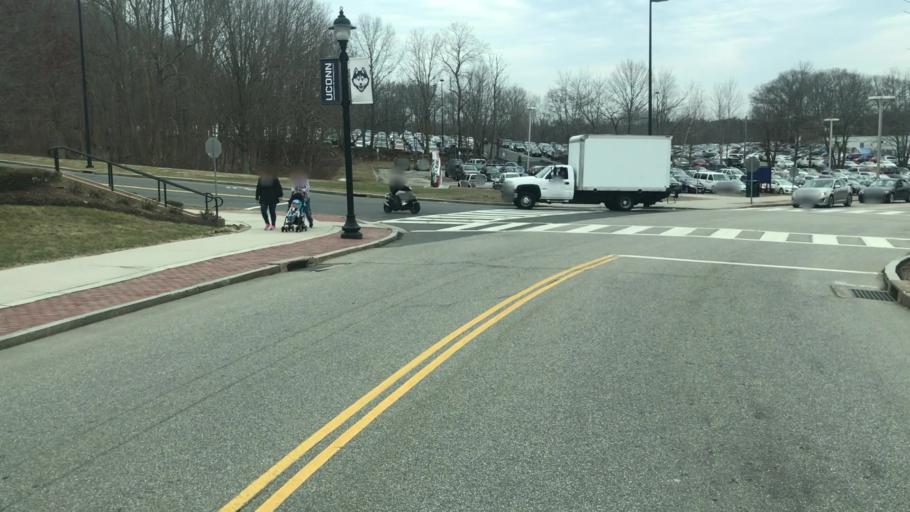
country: US
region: Connecticut
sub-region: Tolland County
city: Storrs
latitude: 41.8082
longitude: -72.2578
